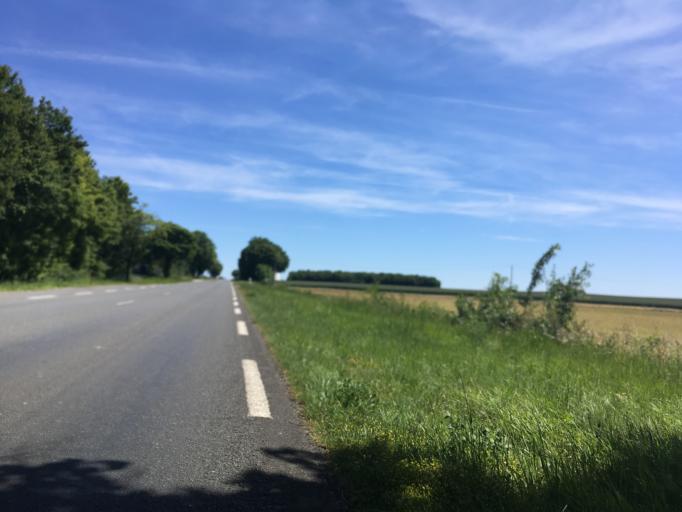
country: FR
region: Poitou-Charentes
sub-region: Departement de la Charente-Maritime
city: Saint-Germain-de-Marencennes
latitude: 46.1069
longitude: -0.7926
